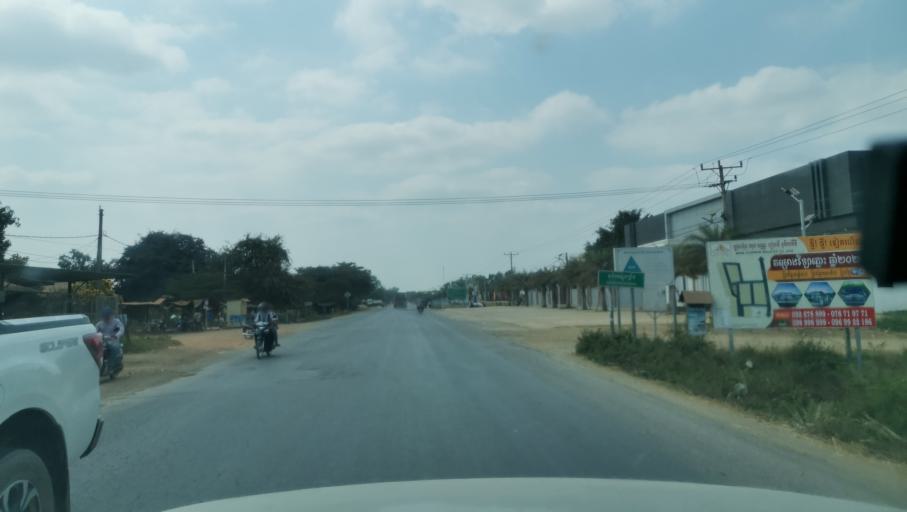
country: KH
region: Battambang
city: Battambang
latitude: 13.0723
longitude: 103.1694
